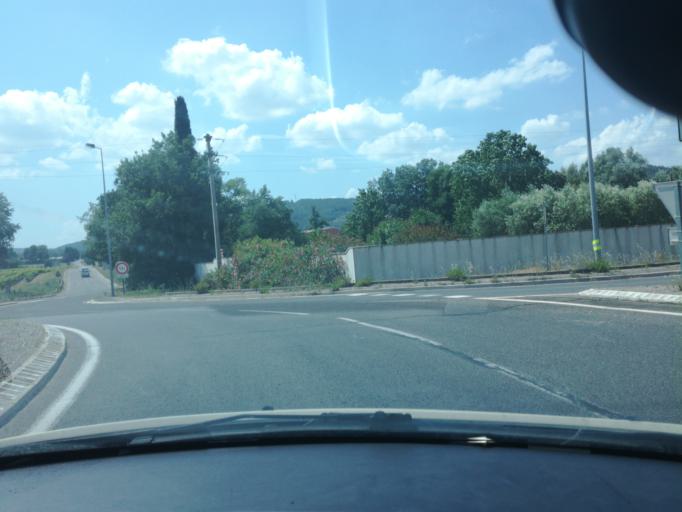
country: FR
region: Provence-Alpes-Cote d'Azur
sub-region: Departement du Var
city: Le Muy
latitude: 43.4931
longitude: 6.5658
